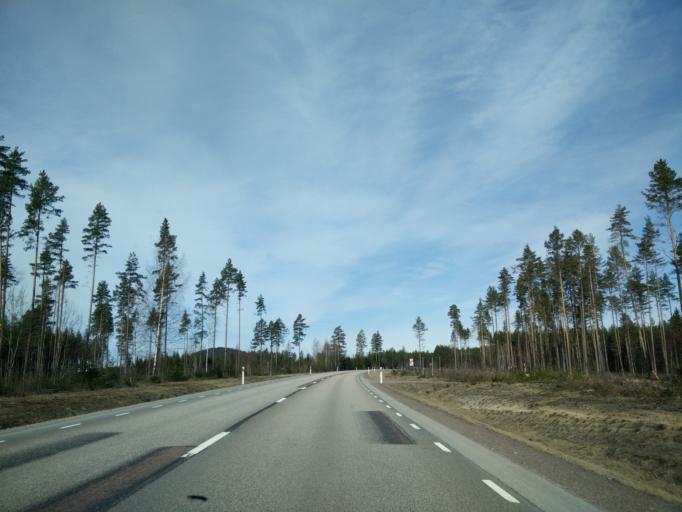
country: SE
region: Vaermland
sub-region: Hagfors Kommun
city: Hagfors
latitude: 60.0194
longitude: 13.5920
